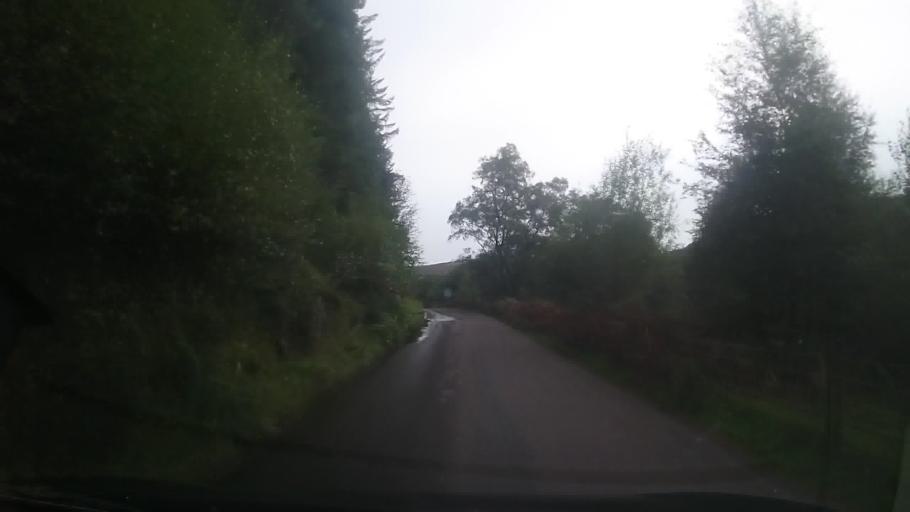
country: GB
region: Wales
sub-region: Sir Powys
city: Rhayader
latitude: 52.2933
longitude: -3.5996
